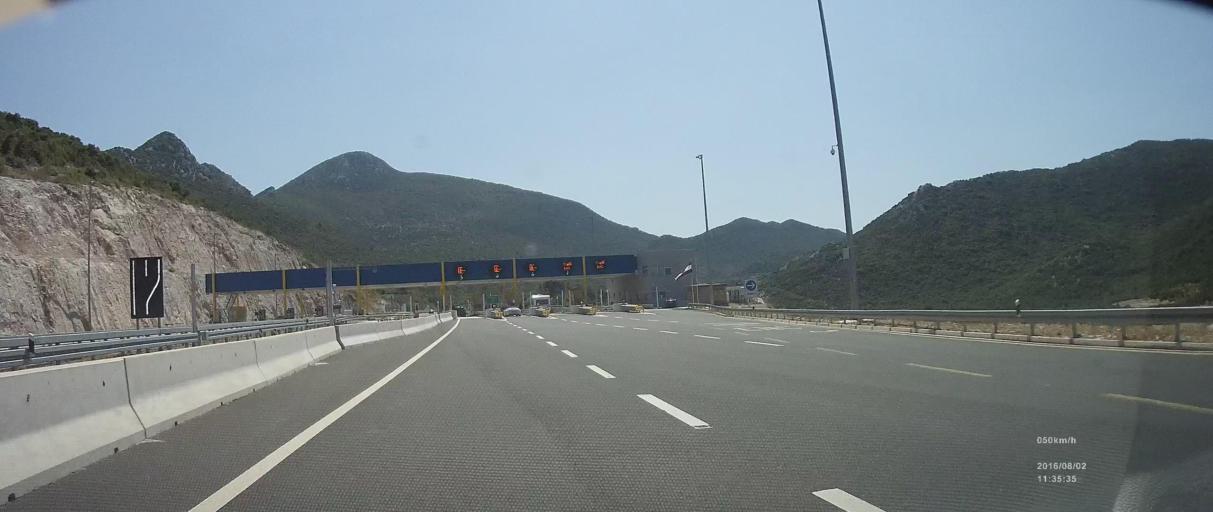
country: HR
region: Dubrovacko-Neretvanska
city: Komin
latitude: 43.1019
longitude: 17.4842
